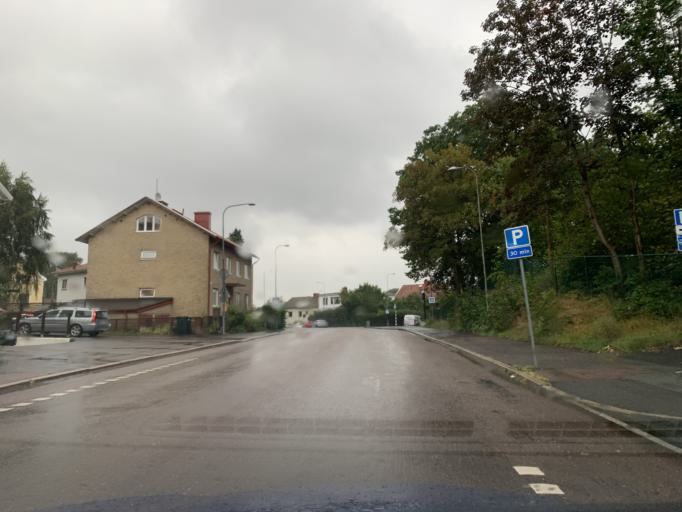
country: SE
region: Vaestra Goetaland
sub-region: Goteborg
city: Goeteborg
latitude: 57.7084
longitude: 12.0133
